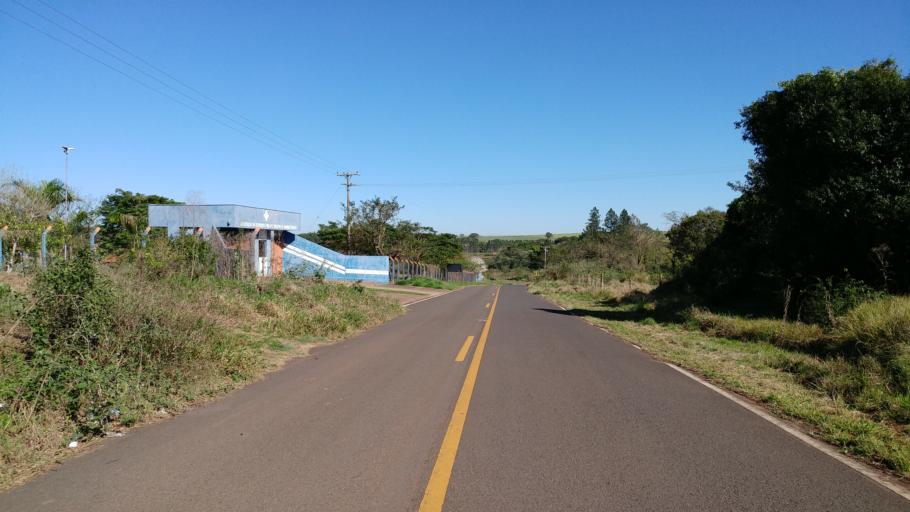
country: BR
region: Sao Paulo
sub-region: Paraguacu Paulista
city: Paraguacu Paulista
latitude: -22.4190
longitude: -50.6082
